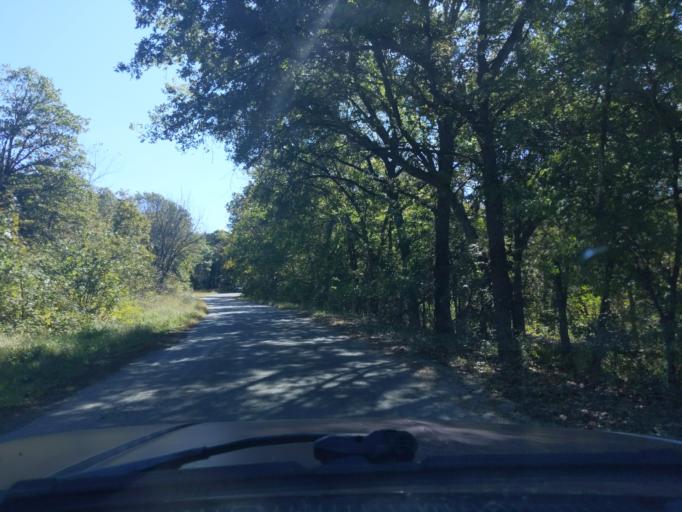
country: US
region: Oklahoma
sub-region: Creek County
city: Bristow
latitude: 35.6874
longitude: -96.4144
